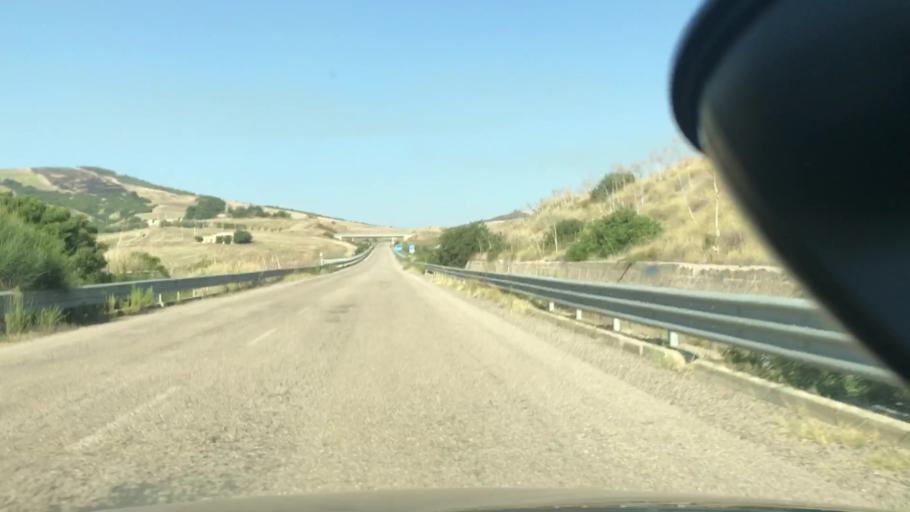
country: IT
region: Basilicate
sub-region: Provincia di Matera
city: La Martella
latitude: 40.6918
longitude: 16.4383
